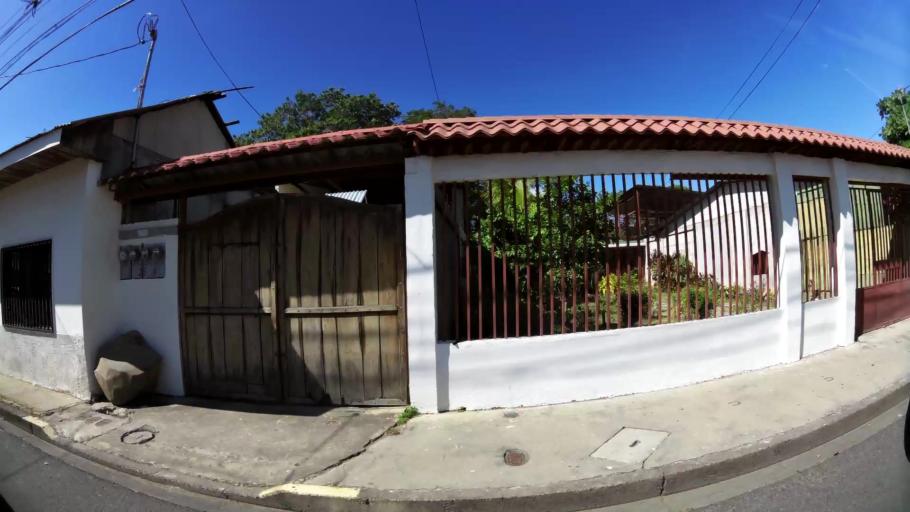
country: CR
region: Guanacaste
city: Liberia
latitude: 10.6346
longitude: -85.4347
